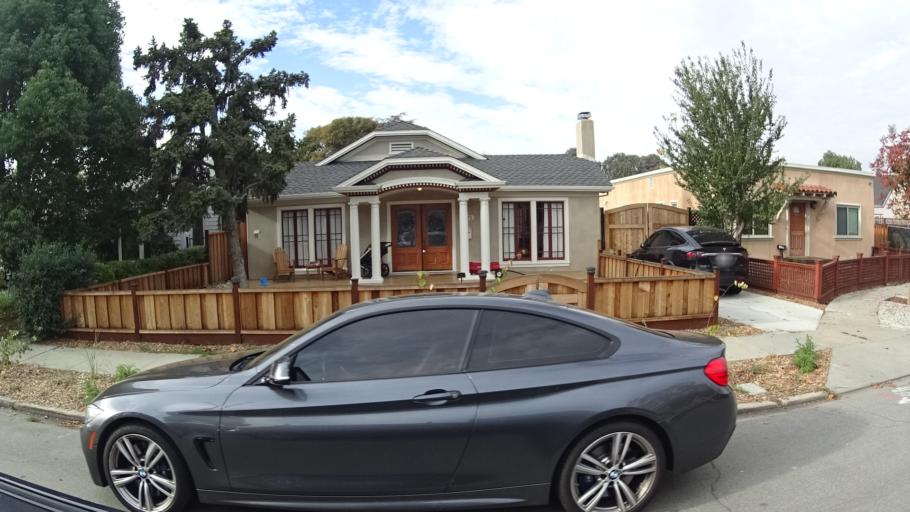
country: US
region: California
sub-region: Santa Clara County
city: Burbank
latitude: 37.3372
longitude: -121.9301
